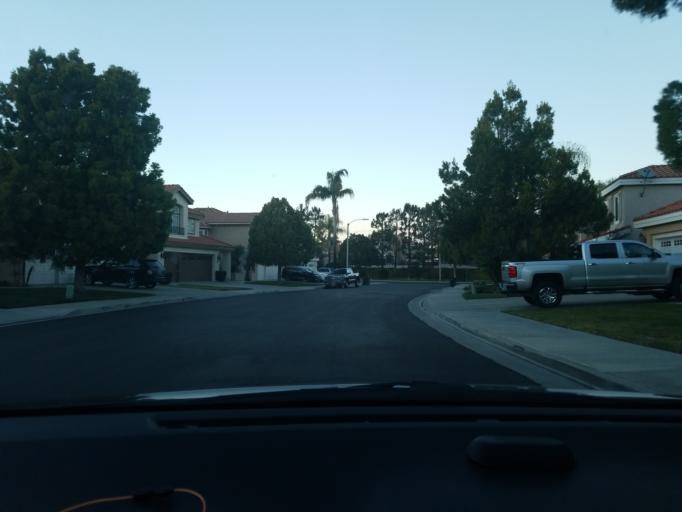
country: US
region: California
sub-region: Riverside County
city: Temecula
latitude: 33.4677
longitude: -117.0940
